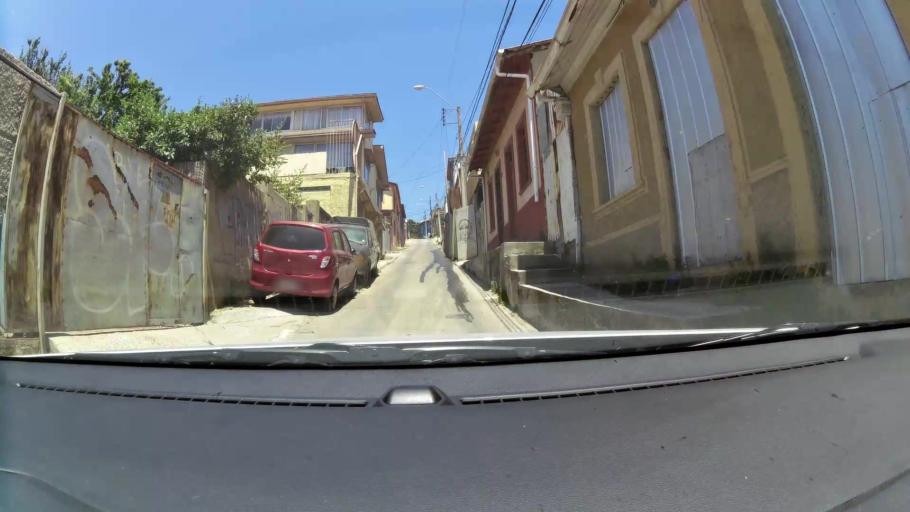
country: CL
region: Valparaiso
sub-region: Provincia de Valparaiso
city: Valparaiso
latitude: -33.0355
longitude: -71.6412
